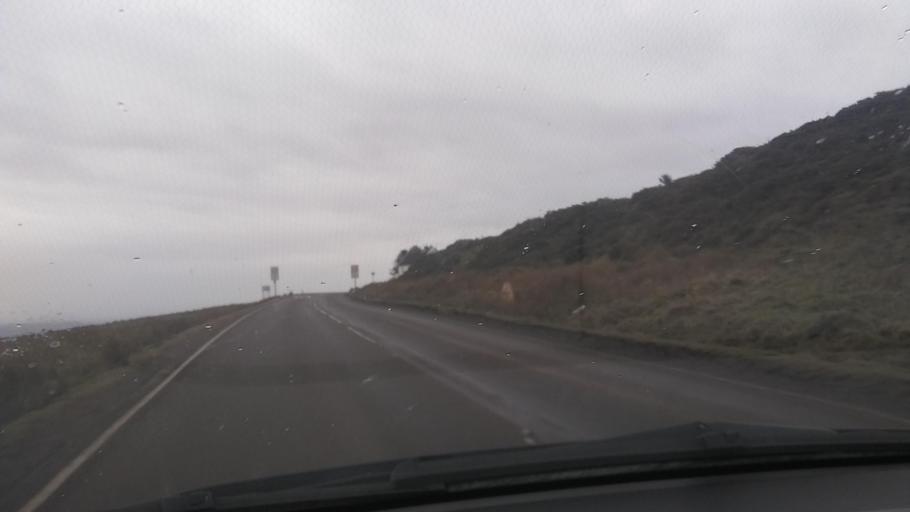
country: GB
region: England
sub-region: Worcestershire
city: Tenbury Wells
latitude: 52.3765
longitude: -2.5915
